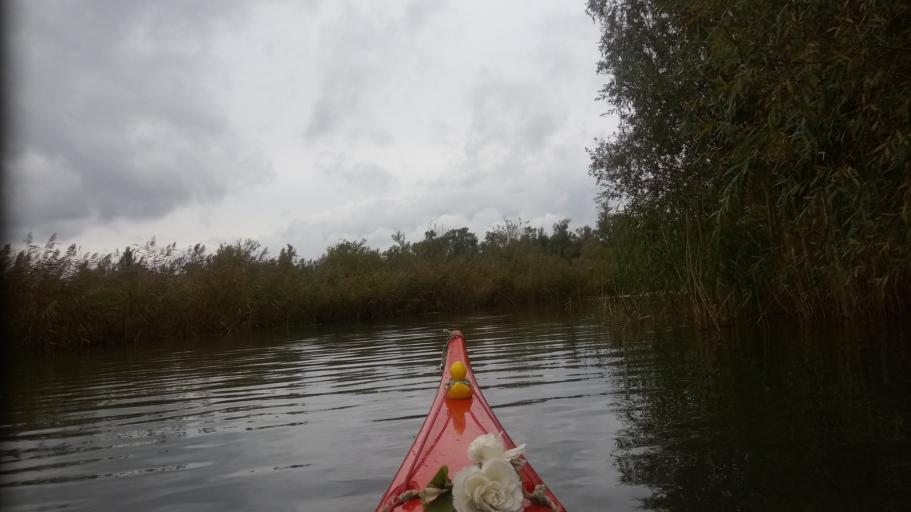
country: NL
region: North Brabant
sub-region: Gemeente Made en Drimmelen
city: Drimmelen
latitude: 51.7517
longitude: 4.7668
